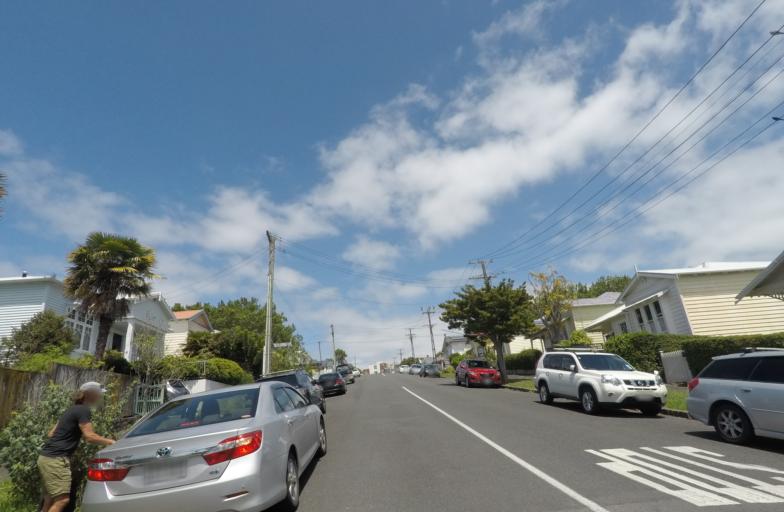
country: NZ
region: Auckland
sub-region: Auckland
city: Auckland
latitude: -36.8619
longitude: 174.7372
